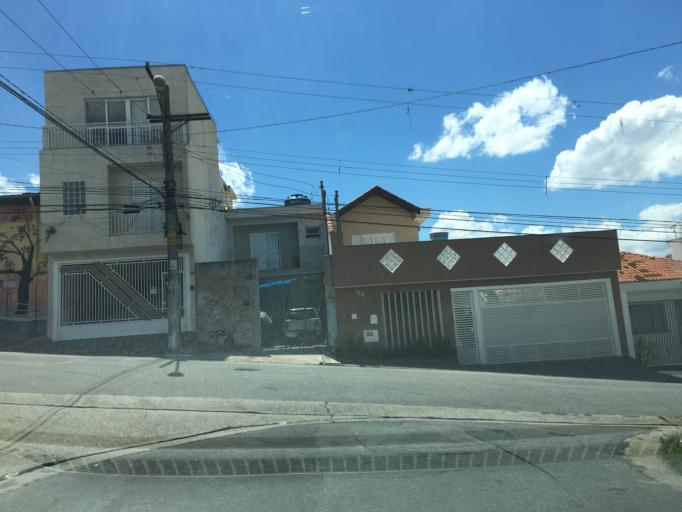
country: BR
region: Sao Paulo
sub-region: Sao Caetano Do Sul
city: Sao Caetano do Sul
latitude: -23.6003
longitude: -46.5331
